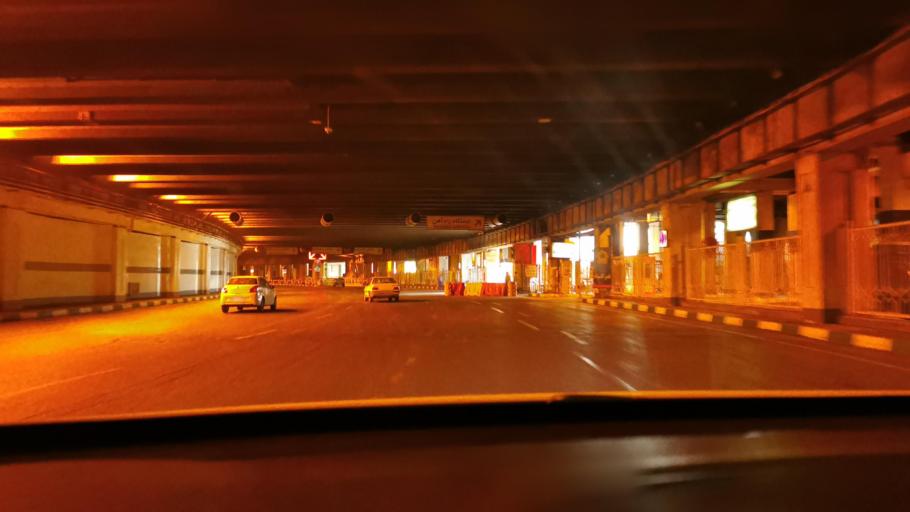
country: IR
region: Razavi Khorasan
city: Mashhad
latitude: 36.2876
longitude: 59.6181
